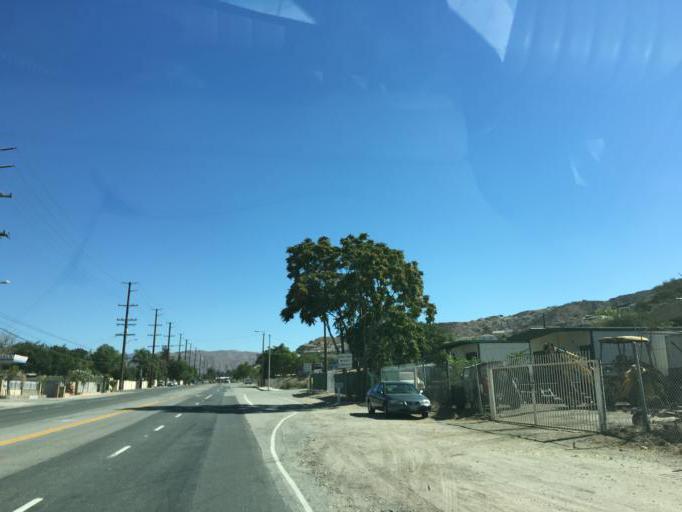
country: US
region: California
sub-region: Los Angeles County
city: Agua Dulce
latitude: 34.4413
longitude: -118.4301
